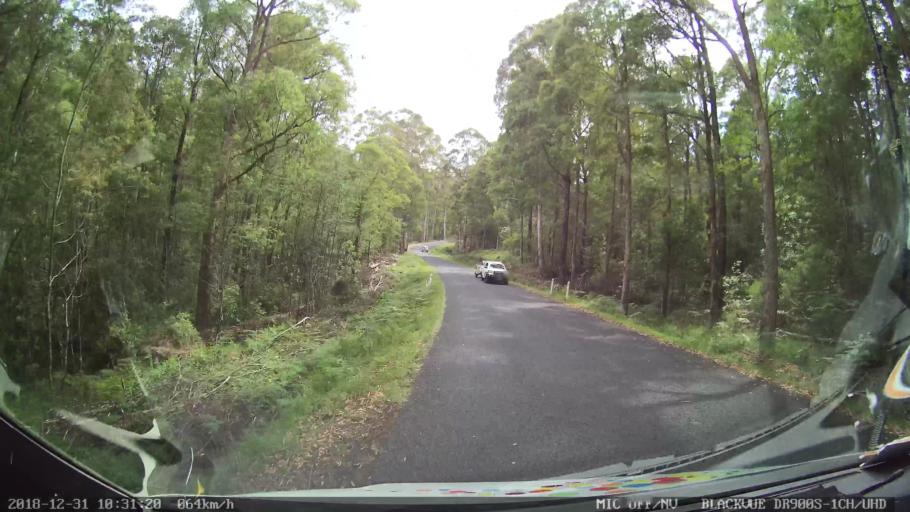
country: AU
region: New South Wales
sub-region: Snowy River
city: Jindabyne
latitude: -36.4583
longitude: 148.1572
